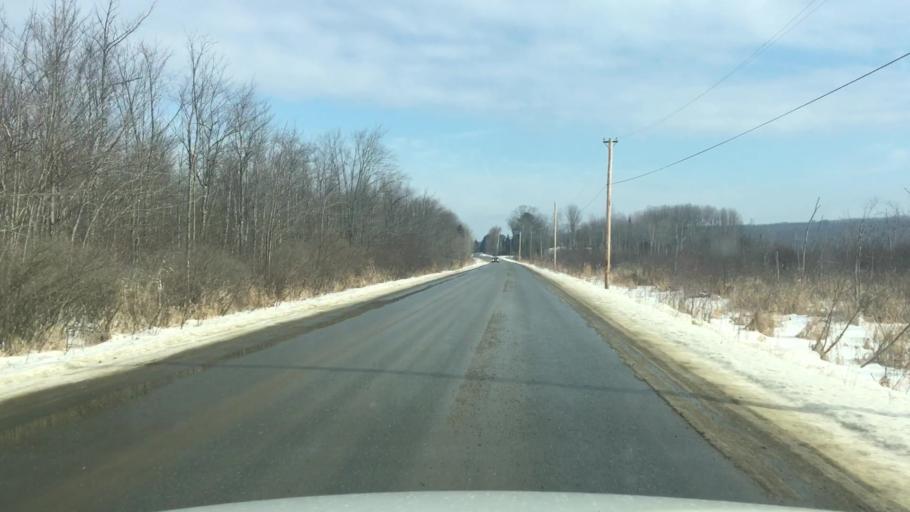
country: US
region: Maine
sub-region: Penobscot County
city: Hermon
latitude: 44.7588
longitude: -68.9635
